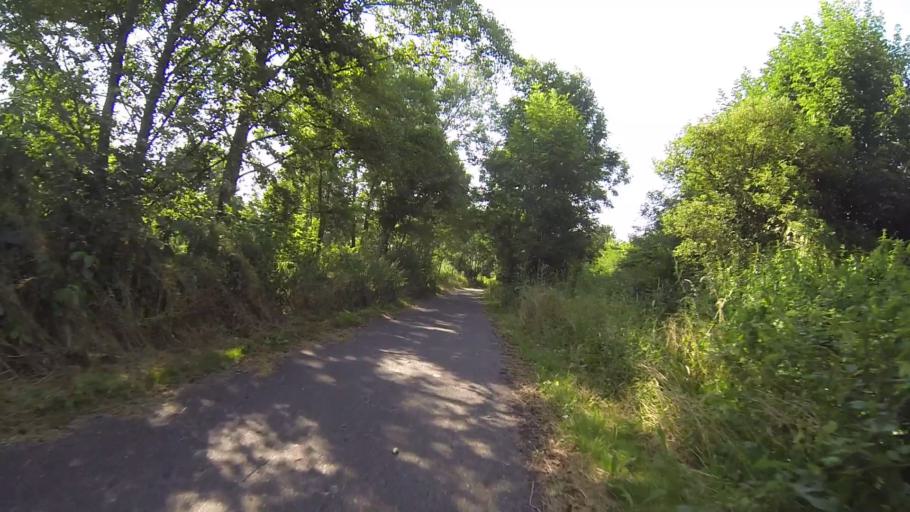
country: DE
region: Baden-Wuerttemberg
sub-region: Tuebingen Region
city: Erbach
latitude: 48.3517
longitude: 9.9247
